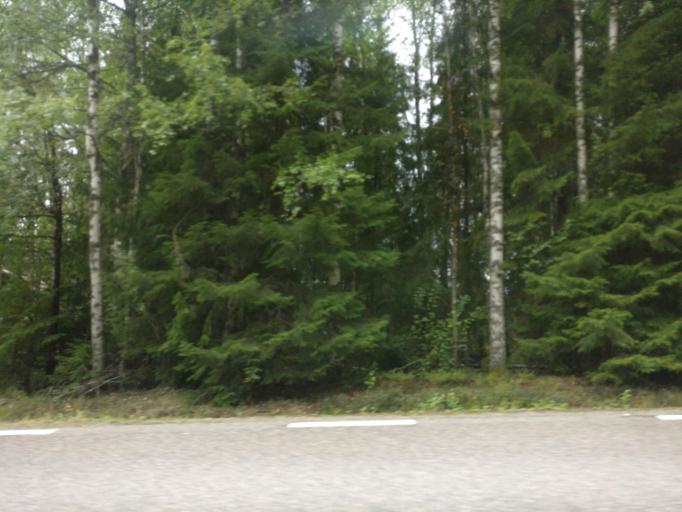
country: SE
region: Vaermland
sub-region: Torsby Kommun
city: Torsby
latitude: 60.7601
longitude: 12.7654
